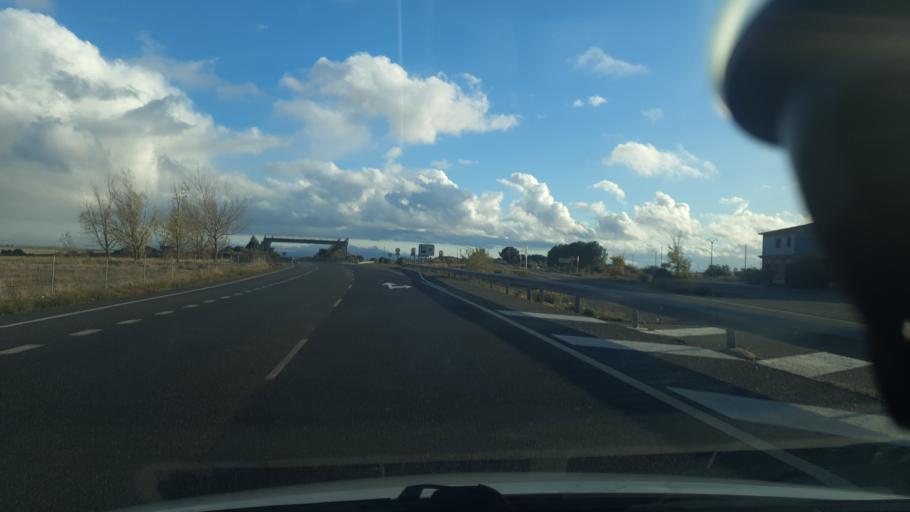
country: ES
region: Castille and Leon
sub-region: Provincia de Segovia
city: Codorniz
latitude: 41.0567
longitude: -4.6302
